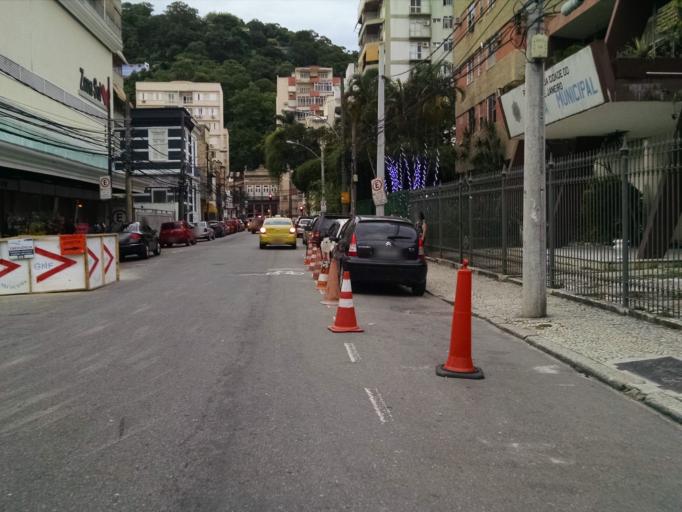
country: BR
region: Rio de Janeiro
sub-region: Rio De Janeiro
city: Rio de Janeiro
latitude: -22.9449
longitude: -43.1854
